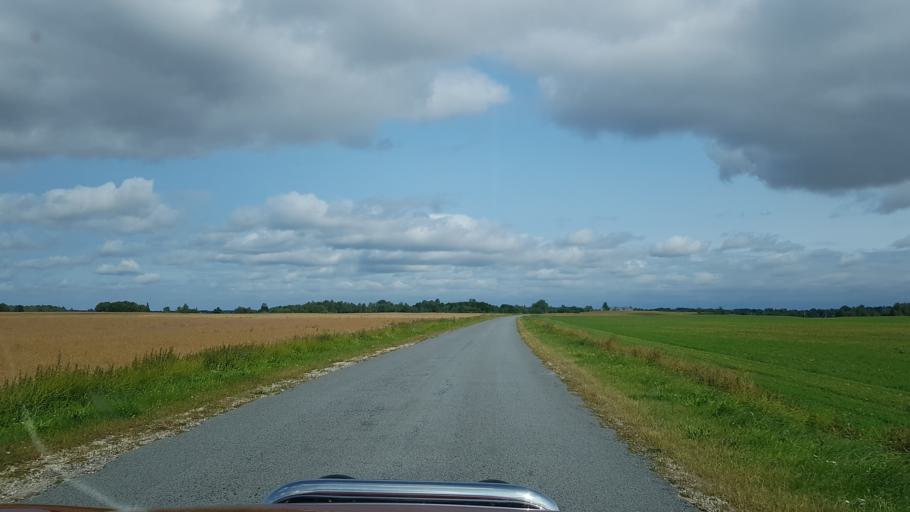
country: EE
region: Laeaene-Virumaa
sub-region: Kadrina vald
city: Kadrina
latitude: 59.3396
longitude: 26.0679
